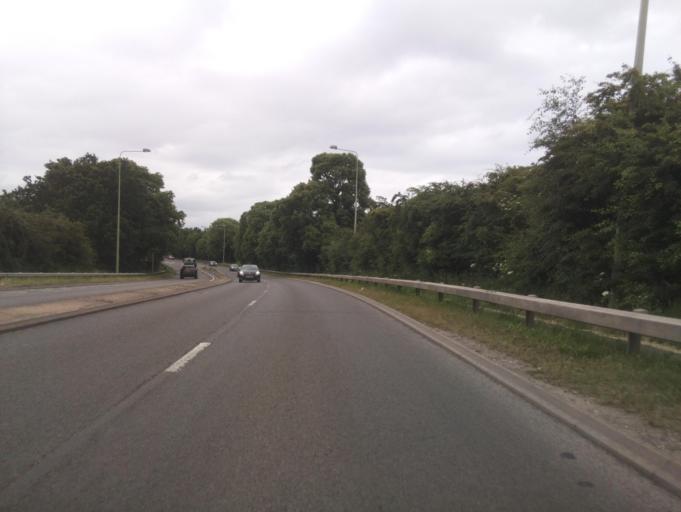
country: GB
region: England
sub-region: Staffordshire
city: Penkridge
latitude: 52.6984
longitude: -2.1283
